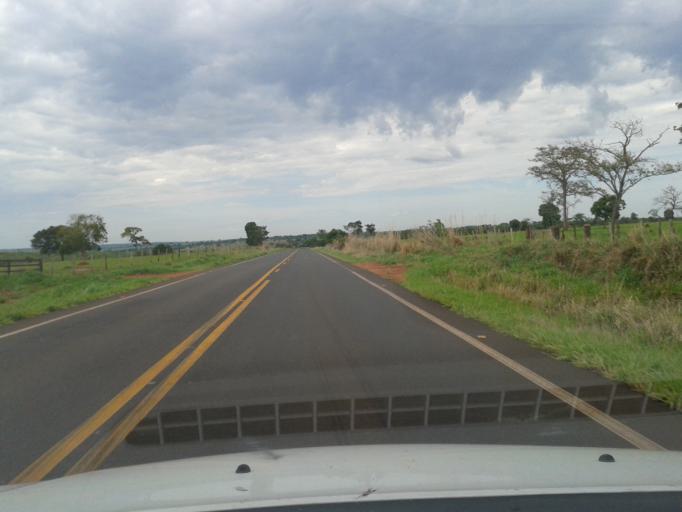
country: BR
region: Minas Gerais
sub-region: Iturama
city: Iturama
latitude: -19.5960
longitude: -50.0408
